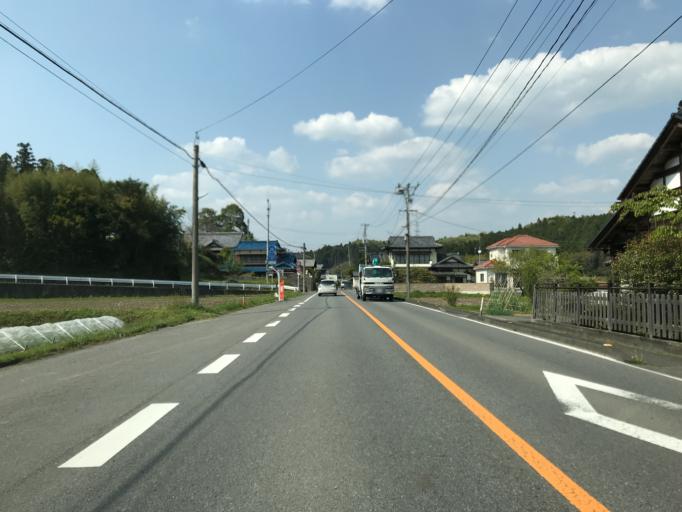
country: JP
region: Fukushima
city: Iwaki
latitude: 36.9493
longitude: 140.7684
